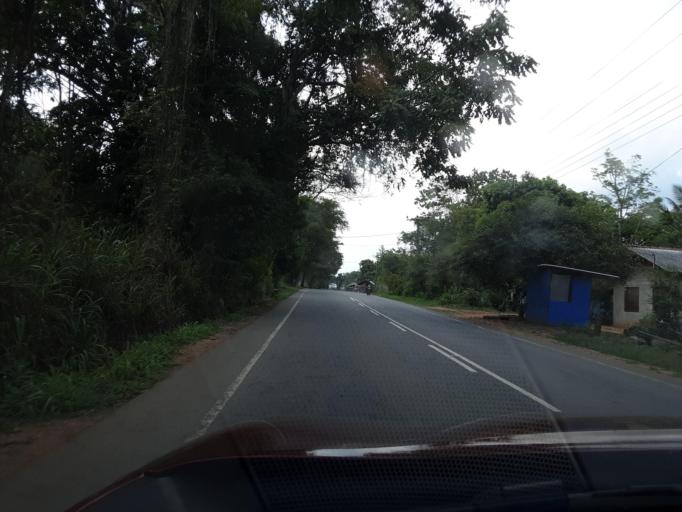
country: LK
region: Uva
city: Haputale
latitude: 6.6973
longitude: 81.1108
